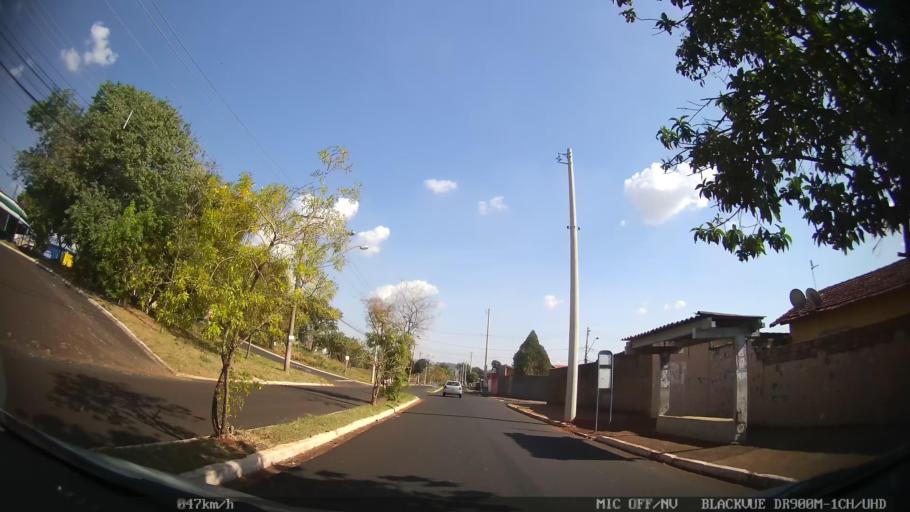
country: BR
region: Sao Paulo
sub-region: Ribeirao Preto
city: Ribeirao Preto
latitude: -21.1940
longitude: -47.8485
